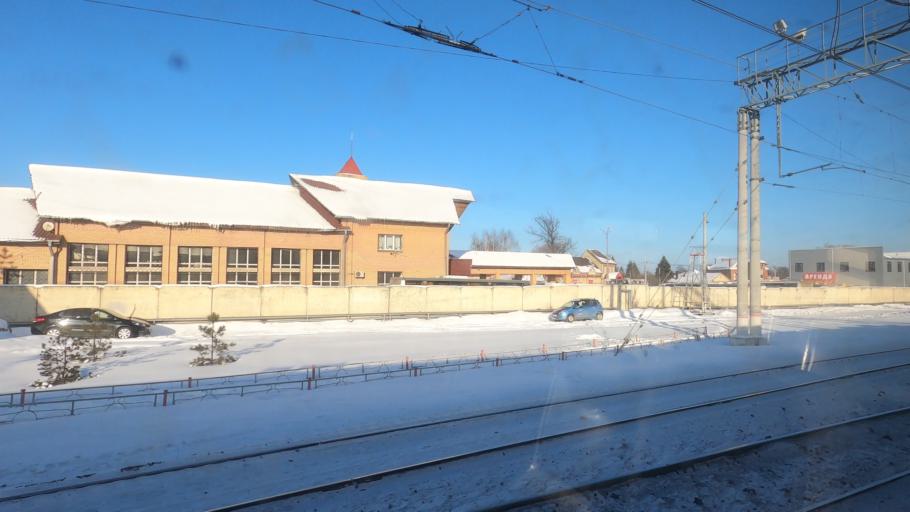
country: RU
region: Moskovskaya
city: Pavlovskiy Posad
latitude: 55.7758
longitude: 38.6771
